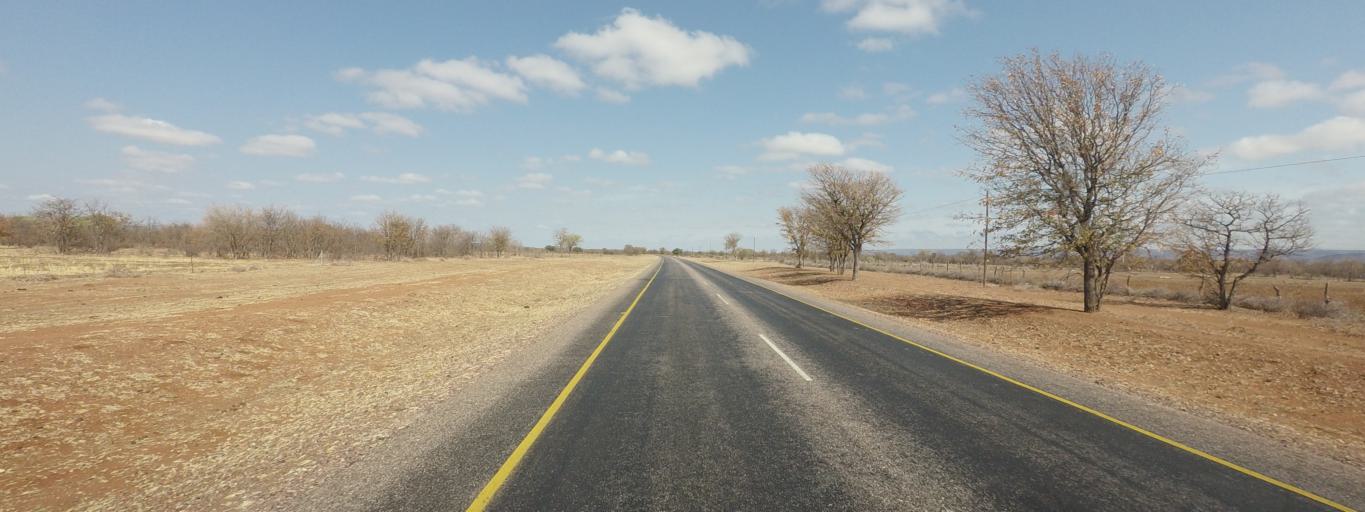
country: BW
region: Central
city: Ramokgonami
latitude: -22.7916
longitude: 27.4567
